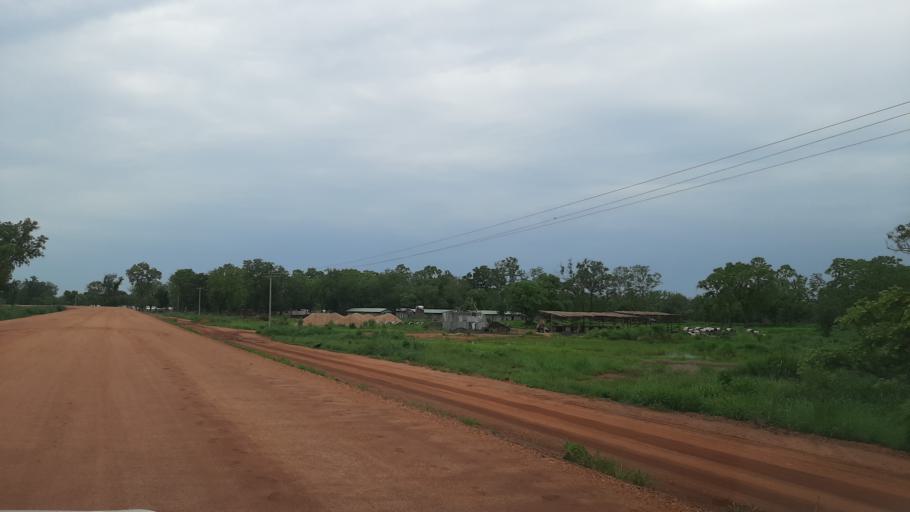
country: ET
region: Gambela
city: Gambela
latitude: 8.1505
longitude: 34.3548
